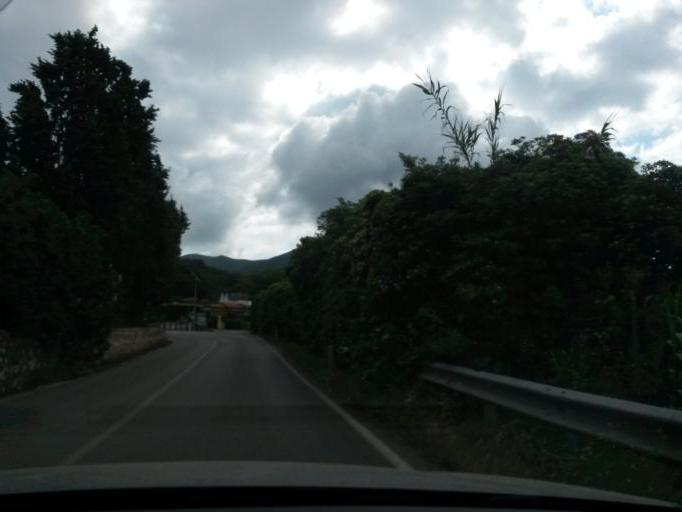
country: IT
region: Tuscany
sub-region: Provincia di Livorno
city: Rio nell'Elba
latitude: 42.7950
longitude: 10.3609
